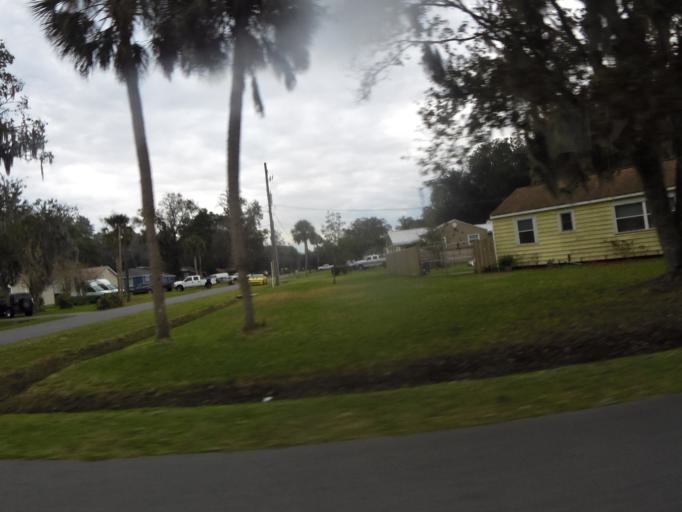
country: US
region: Florida
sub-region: Duval County
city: Jacksonville
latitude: 30.2655
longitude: -81.5958
